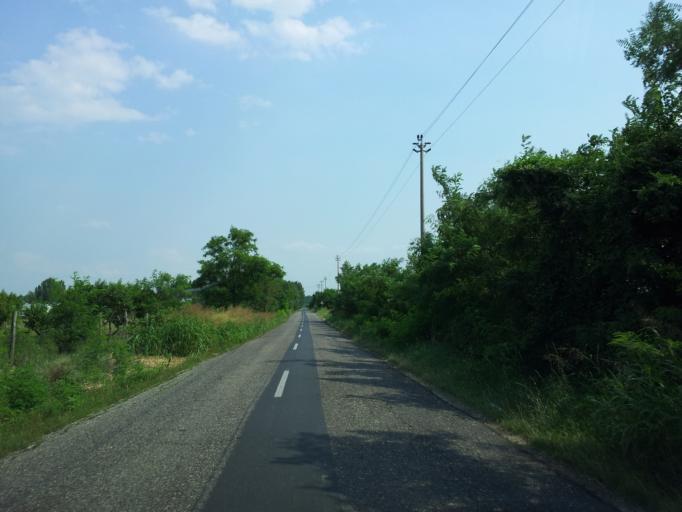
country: HU
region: Pest
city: Rackeve
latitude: 47.1912
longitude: 18.9295
